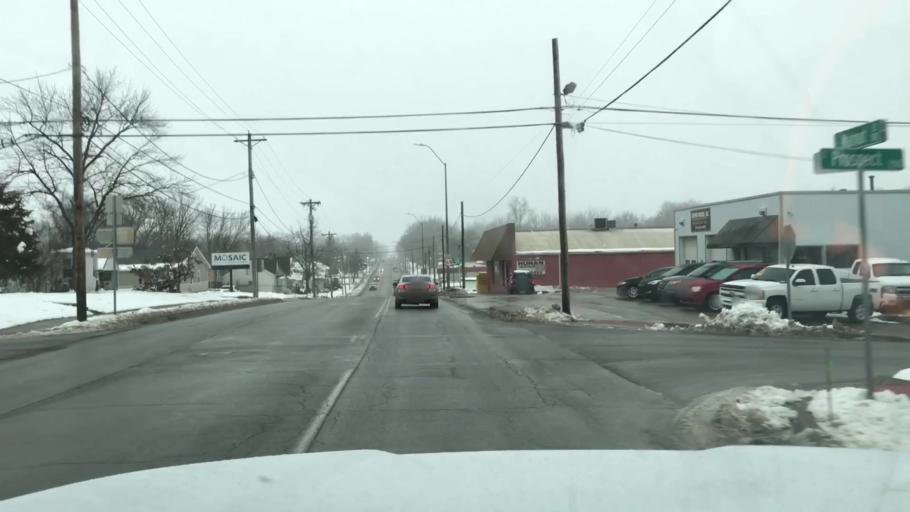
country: US
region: Missouri
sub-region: Clinton County
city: Cameron
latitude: 39.7391
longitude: -94.2360
